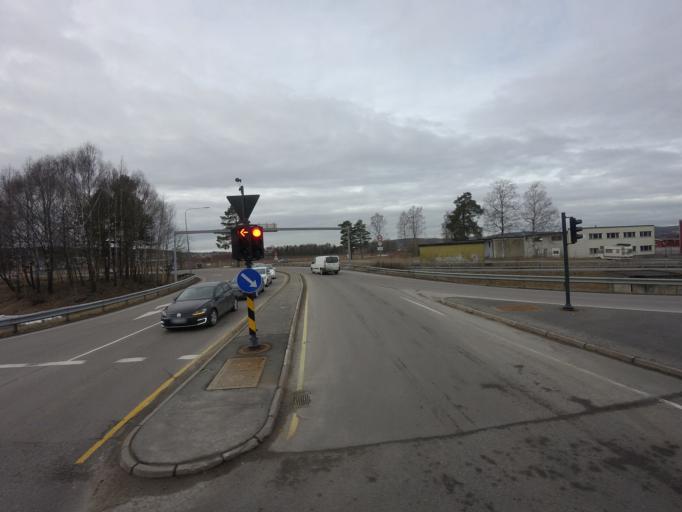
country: NO
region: Akershus
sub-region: Skedsmo
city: Lillestrom
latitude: 59.9676
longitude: 11.0524
